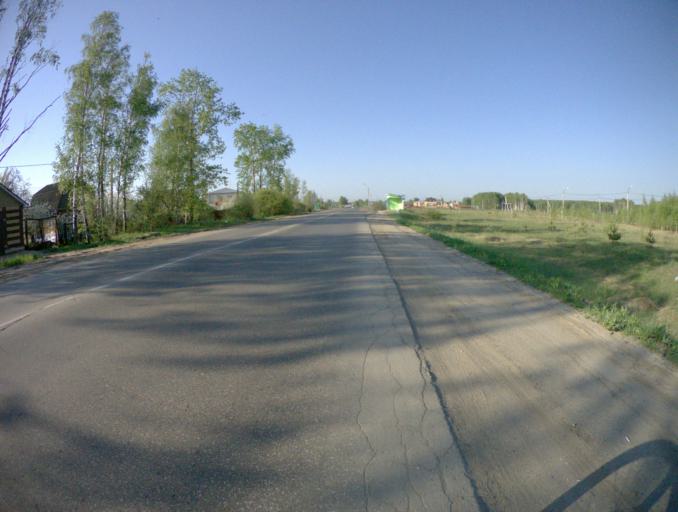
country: RU
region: Vladimir
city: Novovyazniki
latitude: 56.2214
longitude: 42.1855
